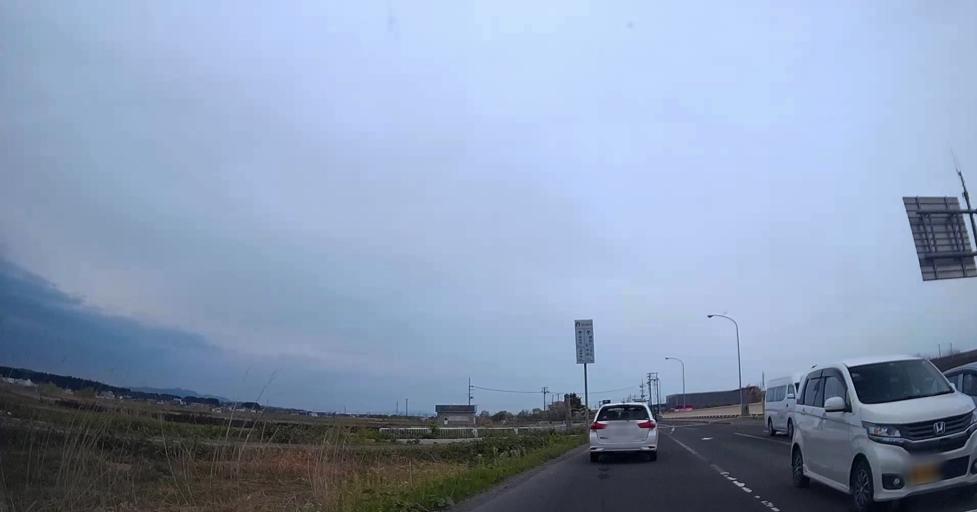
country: JP
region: Aomori
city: Aomori Shi
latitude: 40.8340
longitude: 140.6903
